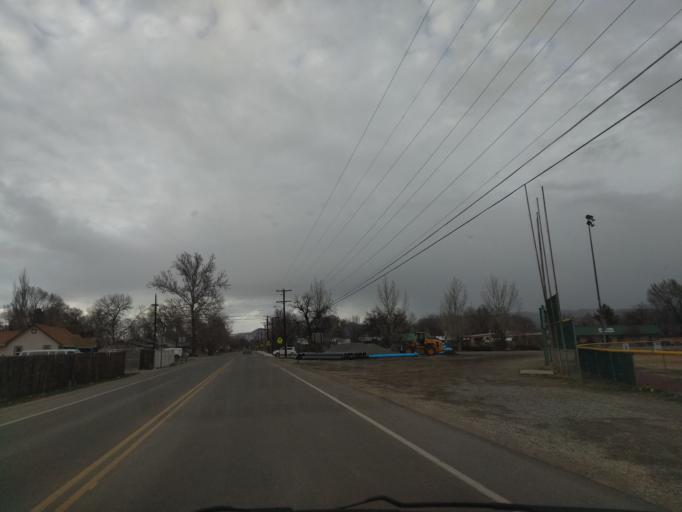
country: US
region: Colorado
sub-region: Mesa County
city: Fruitvale
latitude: 39.0801
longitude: -108.5198
